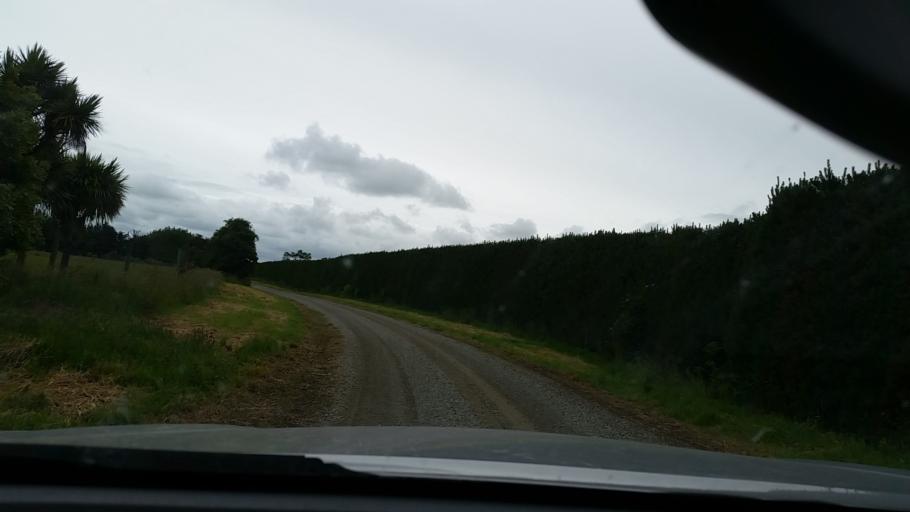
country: NZ
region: Southland
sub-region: Southland District
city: Winton
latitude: -46.1944
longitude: 168.2872
